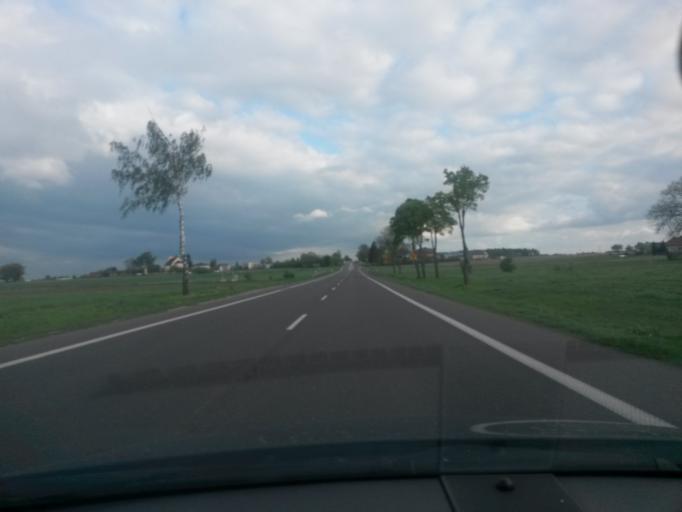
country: PL
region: Masovian Voivodeship
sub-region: Powiat plocki
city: Drobin
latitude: 52.6960
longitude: 20.0445
